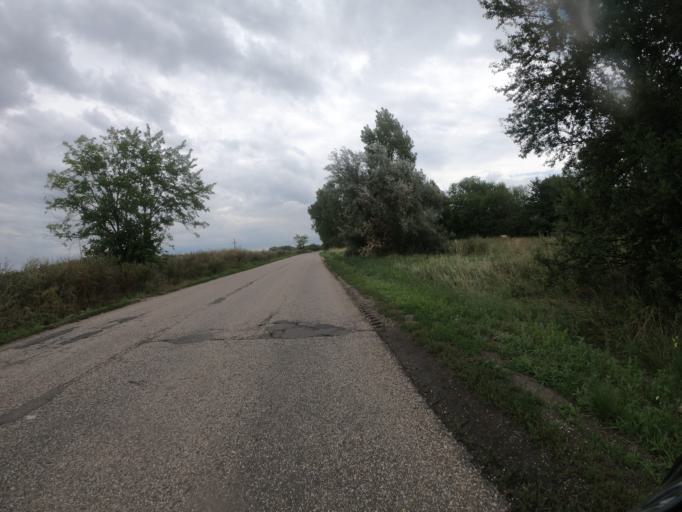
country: HU
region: Borsod-Abauj-Zemplen
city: Szentistvan
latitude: 47.7863
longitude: 20.6293
